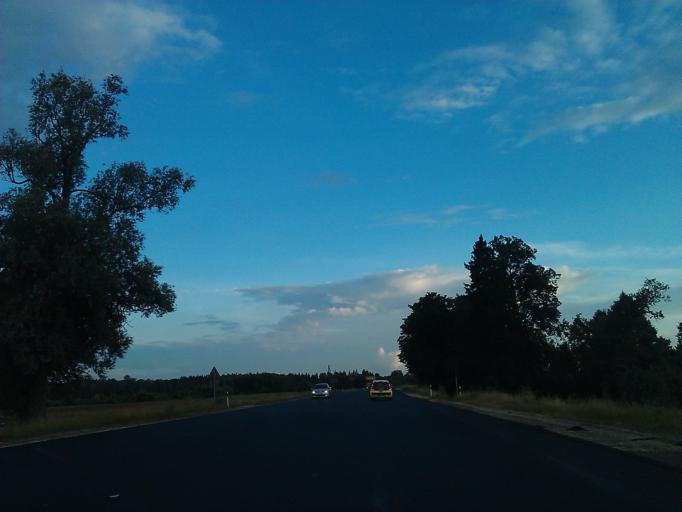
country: LV
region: Adazi
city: Adazi
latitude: 57.1160
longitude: 24.3234
